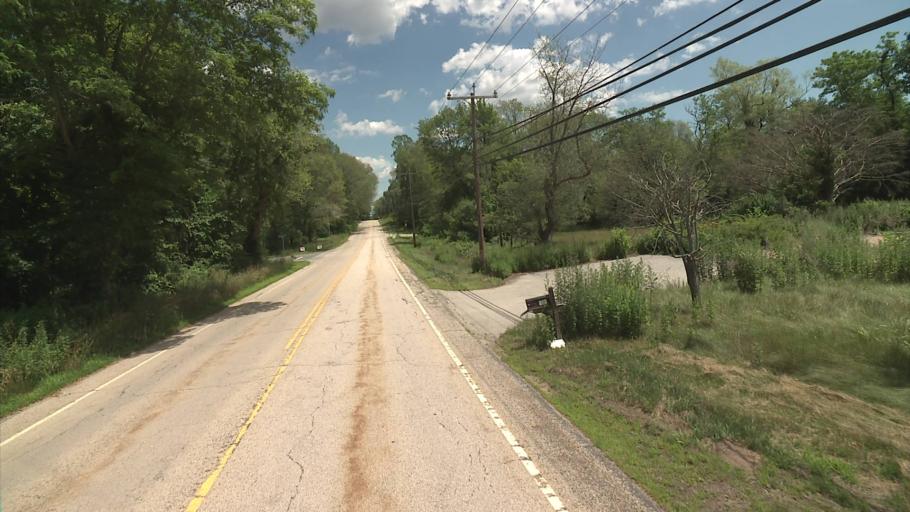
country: US
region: Connecticut
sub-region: Middlesex County
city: Moodus
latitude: 41.4710
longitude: -72.3997
